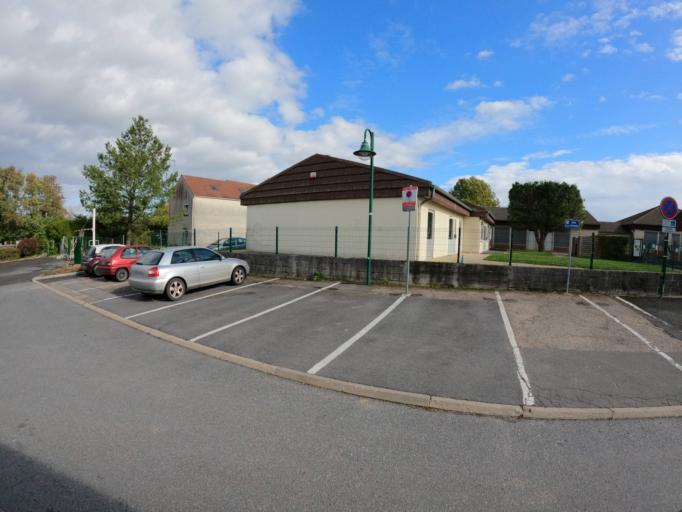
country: FR
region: Ile-de-France
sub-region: Departement de Seine-et-Marne
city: Montry
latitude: 48.8844
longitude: 2.8325
